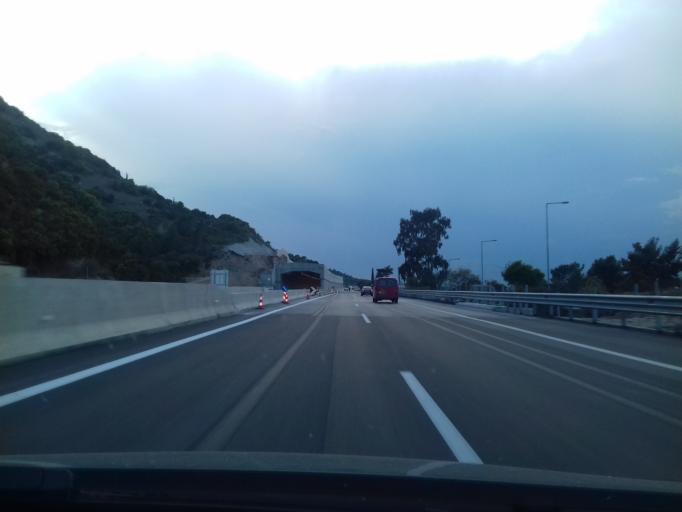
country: GR
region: West Greece
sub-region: Nomos Achaias
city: Ano Kastritsion
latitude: 38.3233
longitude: 21.8831
